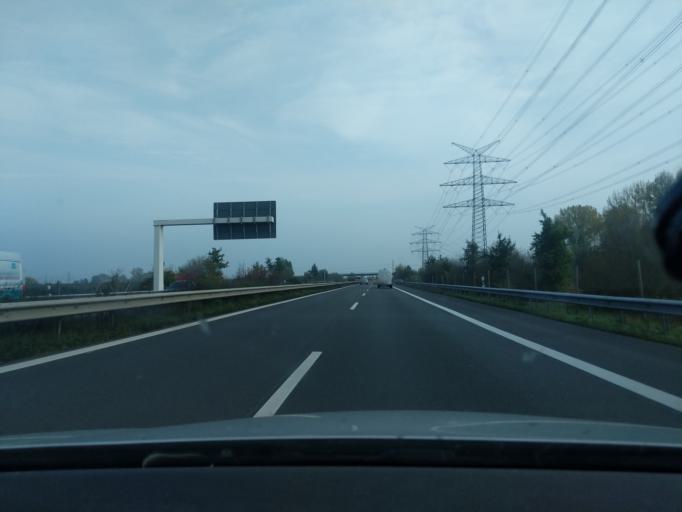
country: DE
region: Lower Saxony
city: Agathenburg
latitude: 53.5749
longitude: 9.5375
